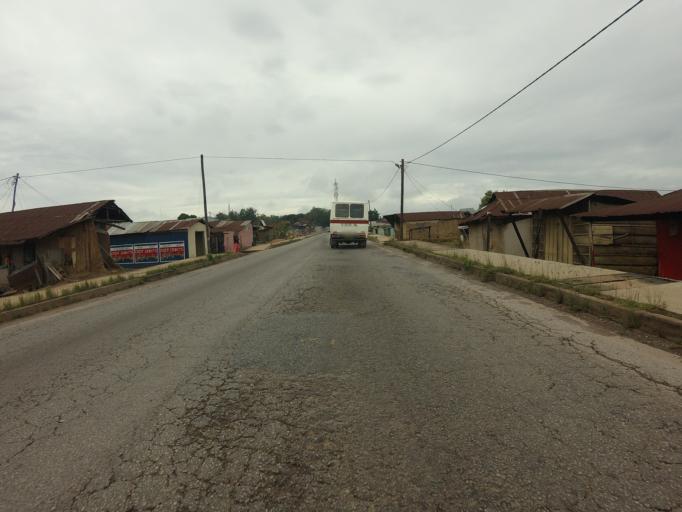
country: GH
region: Eastern
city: Begoro
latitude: 6.4333
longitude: -0.5844
